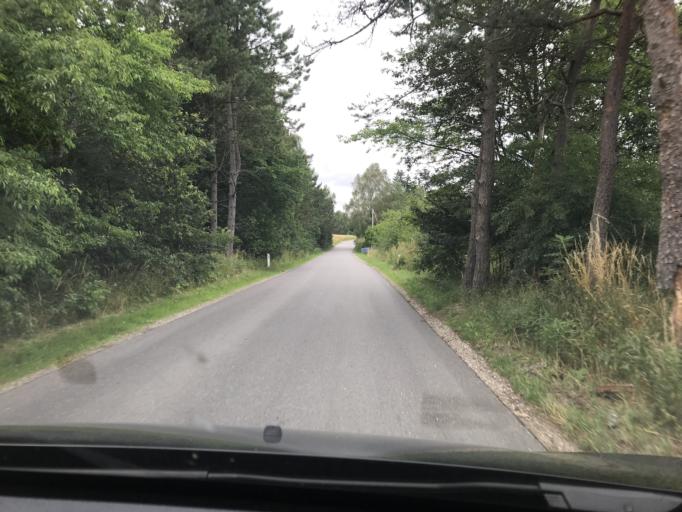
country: DK
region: Central Jutland
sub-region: Syddjurs Kommune
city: Ryomgard
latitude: 56.3657
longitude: 10.4437
